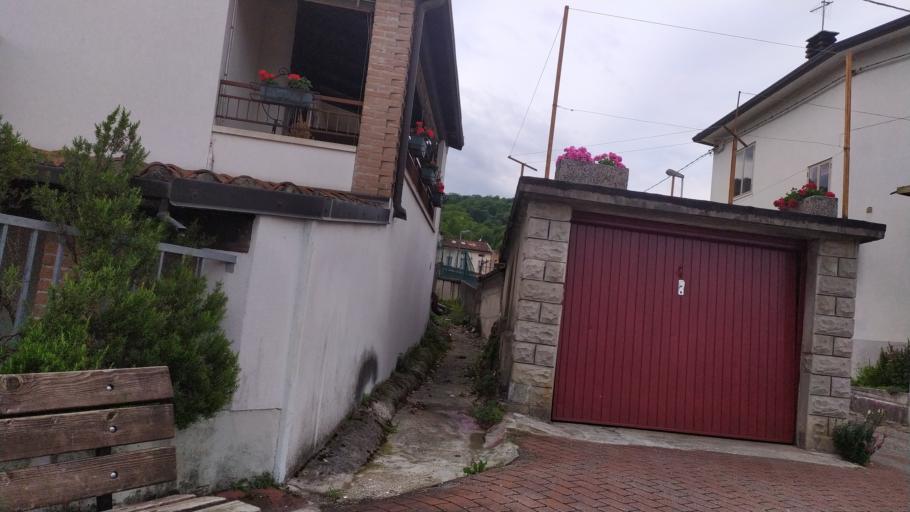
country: IT
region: Veneto
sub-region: Provincia di Vicenza
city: Schio
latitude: 45.7026
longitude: 11.3428
